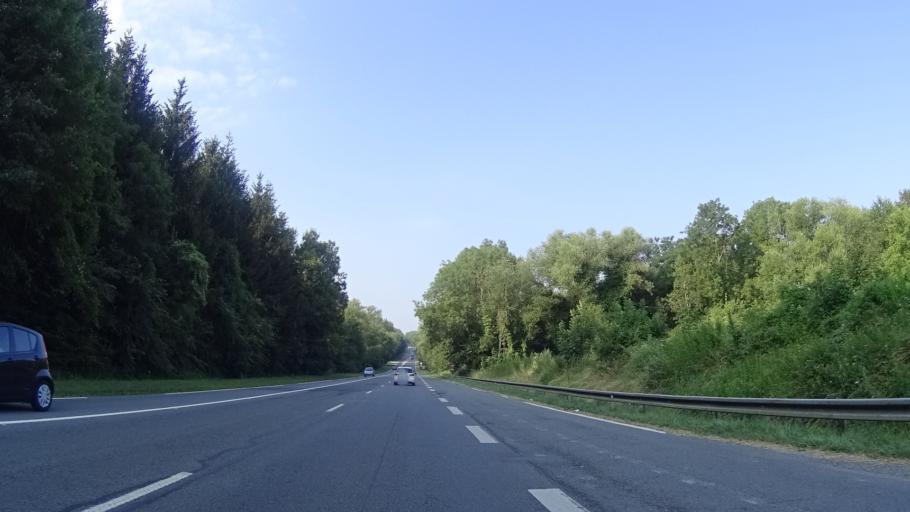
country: FR
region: Ile-de-France
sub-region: Departement du Val-d'Oise
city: Luzarches
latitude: 49.1086
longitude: 2.4279
